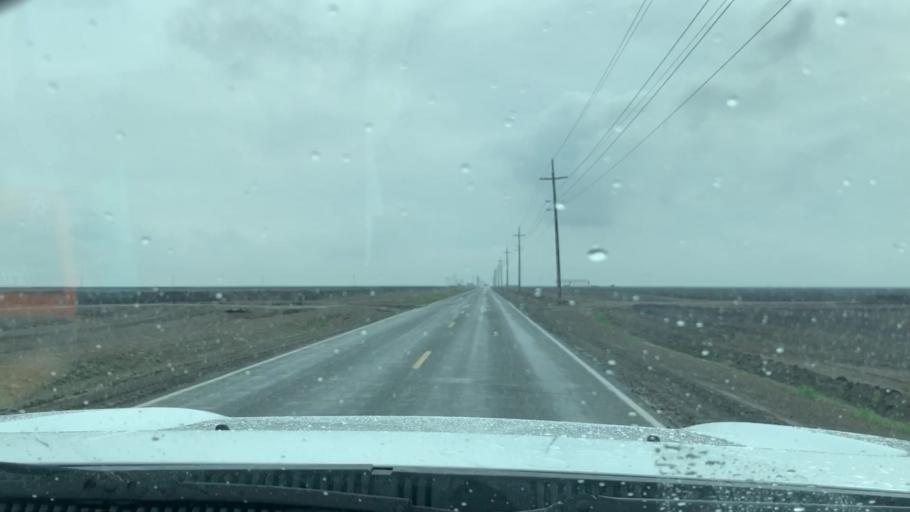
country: US
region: California
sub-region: Kings County
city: Corcoran
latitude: 36.0004
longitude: -119.5721
